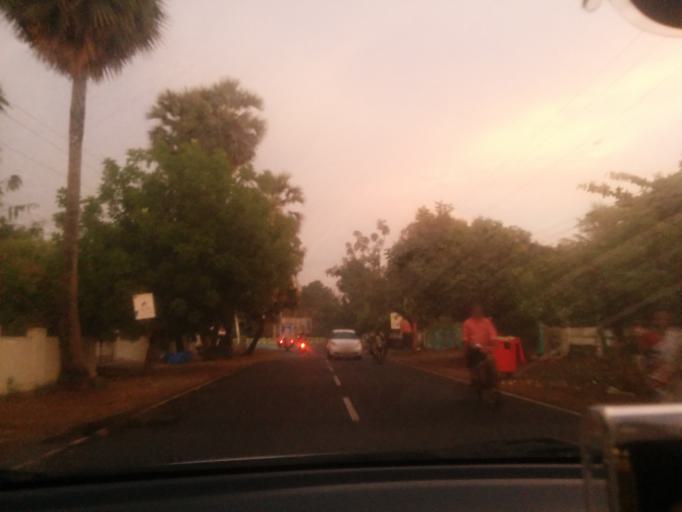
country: IN
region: Andhra Pradesh
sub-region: East Godavari
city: Rajahmundry
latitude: 17.0208
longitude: 81.7938
